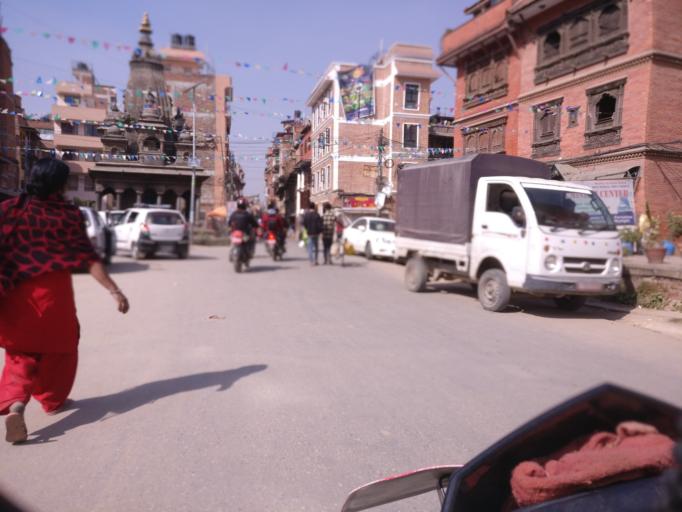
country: NP
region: Central Region
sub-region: Bagmati Zone
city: Patan
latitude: 27.6696
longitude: 85.3282
